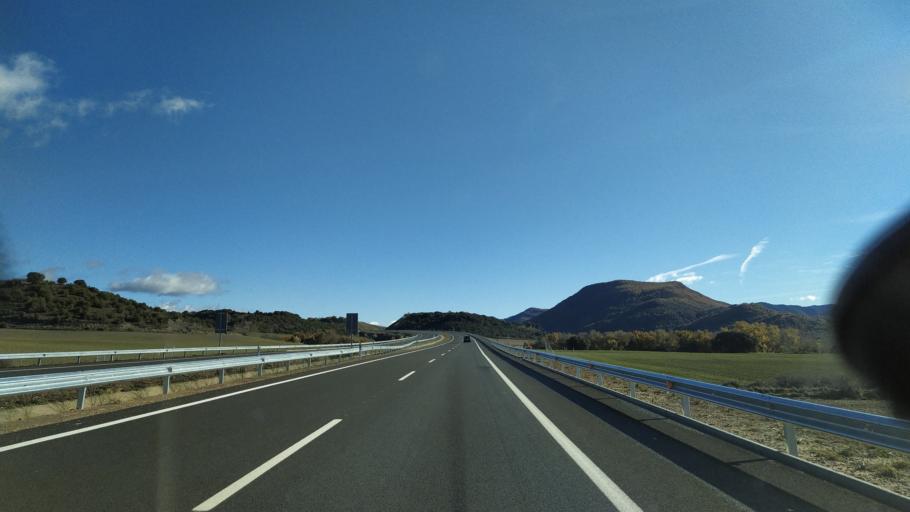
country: ES
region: Aragon
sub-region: Provincia de Huesca
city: Santa Cruz de la Seros
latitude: 42.5643
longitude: -0.6969
